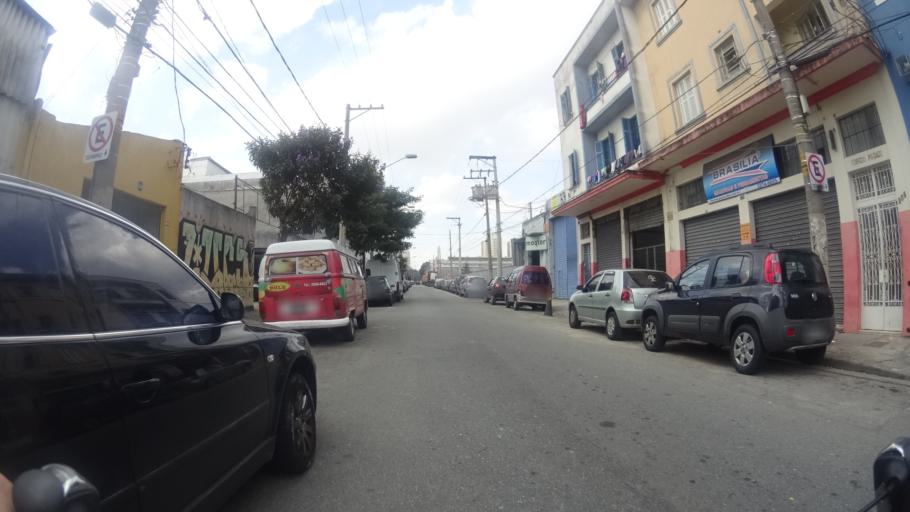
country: BR
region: Sao Paulo
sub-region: Sao Paulo
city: Sao Paulo
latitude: -23.5512
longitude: -46.6166
